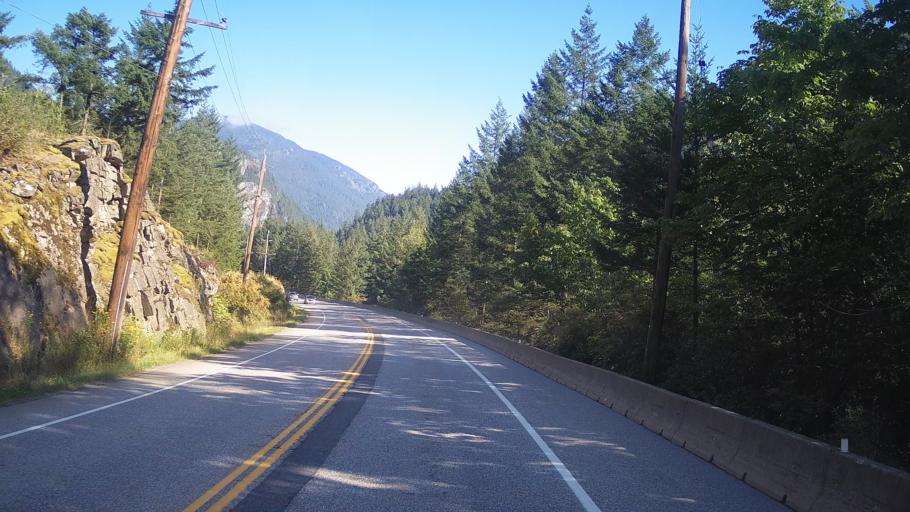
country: CA
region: British Columbia
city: Hope
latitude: 49.6311
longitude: -121.3931
